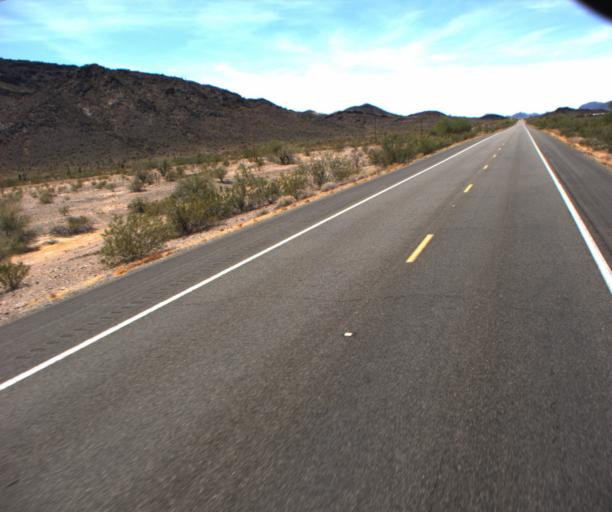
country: US
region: Arizona
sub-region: La Paz County
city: Salome
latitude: 33.6879
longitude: -113.9118
